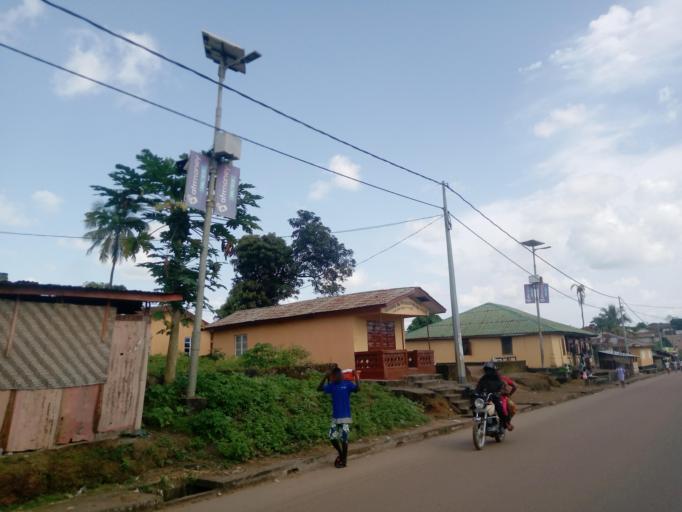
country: SL
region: Northern Province
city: Makeni
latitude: 8.8942
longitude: -12.0379
